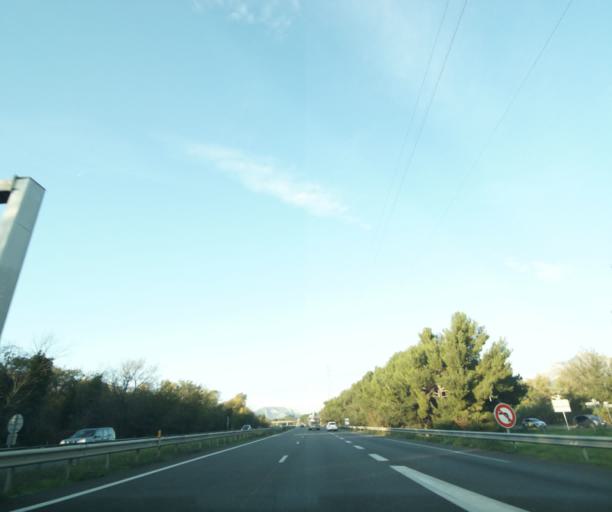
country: FR
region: Provence-Alpes-Cote d'Azur
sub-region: Departement des Bouches-du-Rhone
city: Aubagne
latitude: 43.3013
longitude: 5.5909
